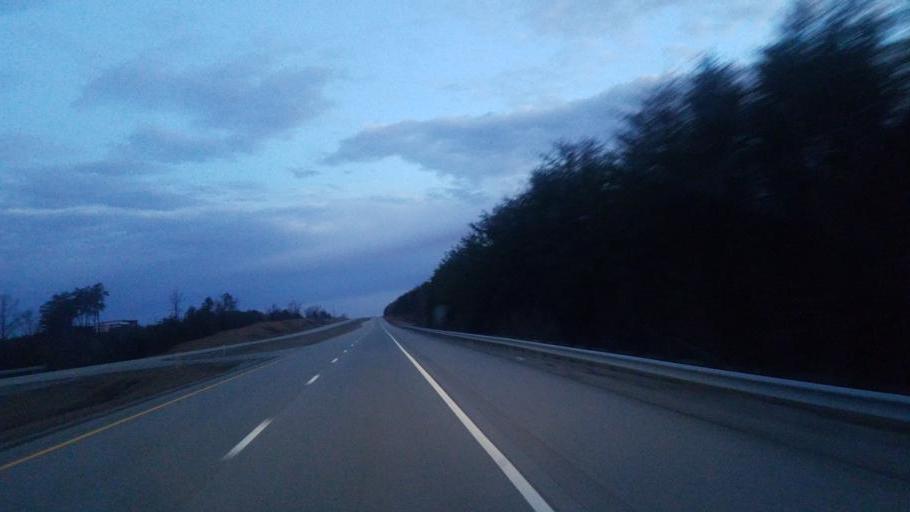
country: US
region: Tennessee
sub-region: Van Buren County
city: Spencer
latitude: 35.6491
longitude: -85.4736
